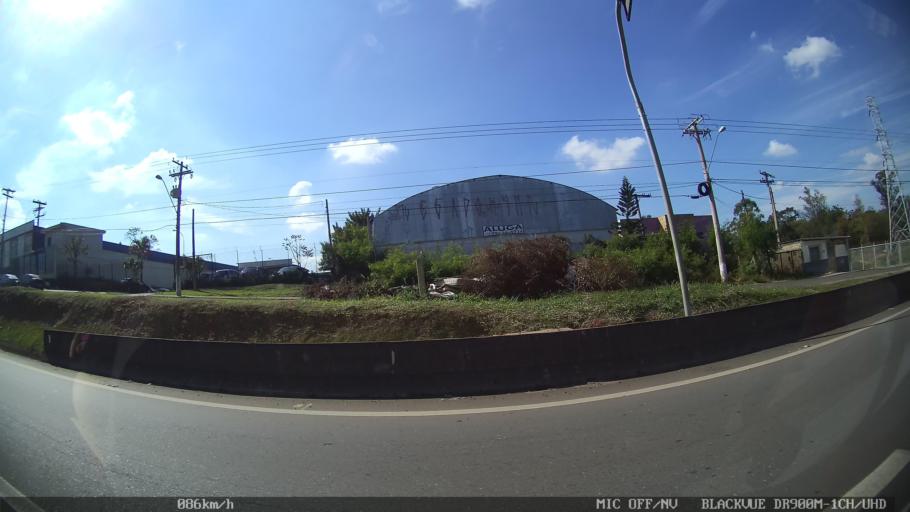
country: BR
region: Sao Paulo
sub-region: Hortolandia
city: Hortolandia
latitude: -22.8345
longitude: -47.1749
